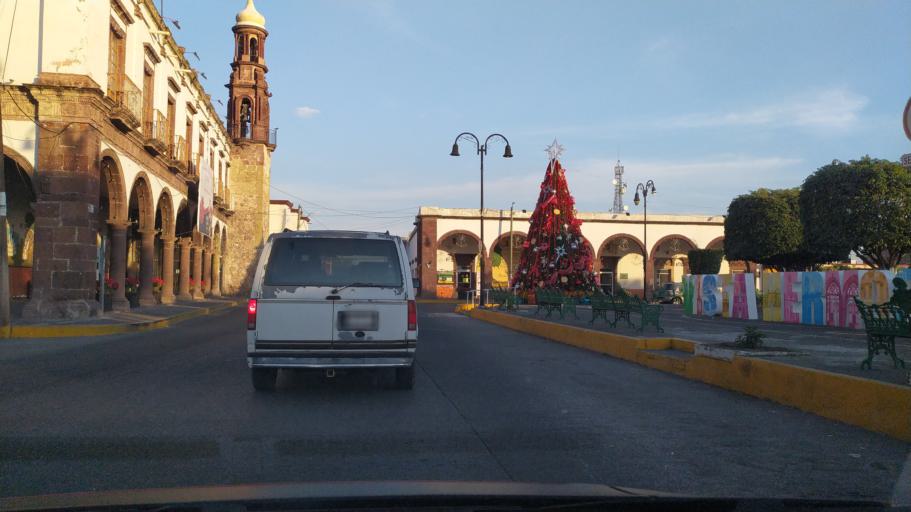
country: MX
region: Michoacan
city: Vistahermosa de Negrete
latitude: 20.2729
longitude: -102.4740
